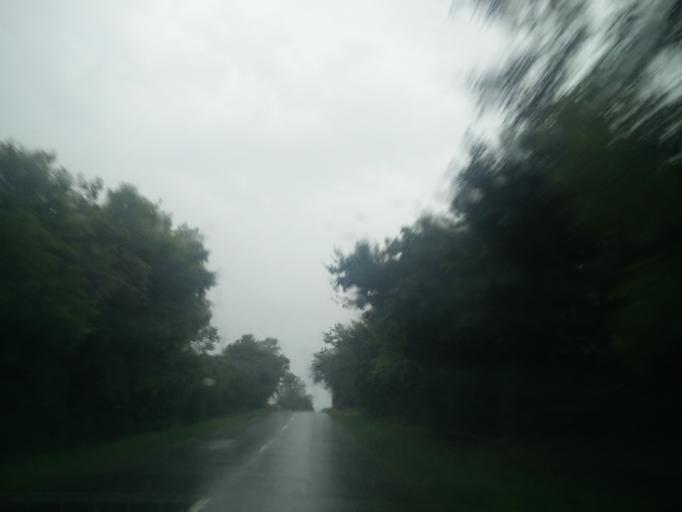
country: HU
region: Fejer
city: Etyek
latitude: 47.4449
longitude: 18.7233
